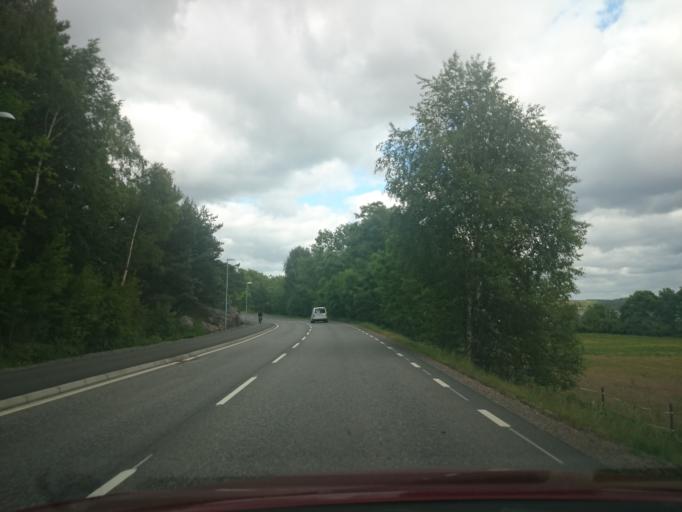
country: SE
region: Vaestra Goetaland
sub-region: Harryda Kommun
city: Molnlycke
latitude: 57.6720
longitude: 12.0661
